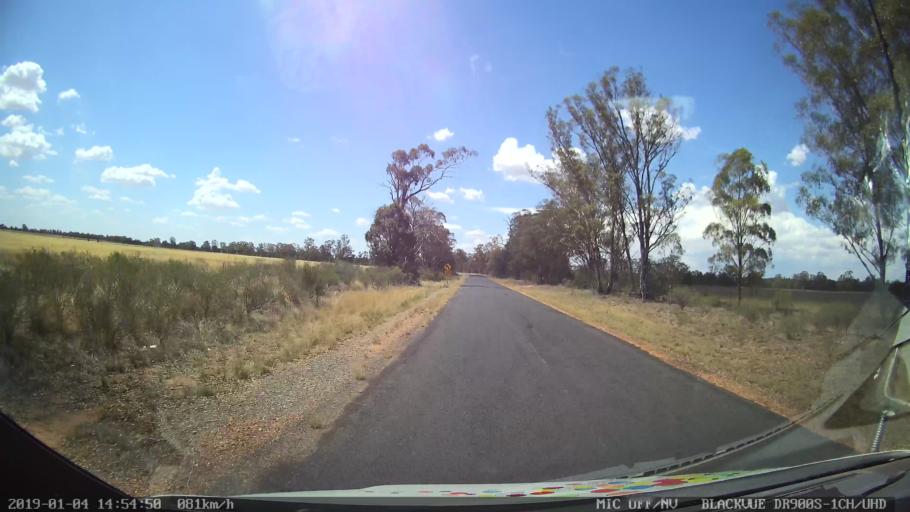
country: AU
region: New South Wales
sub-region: Dubbo Municipality
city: Dubbo
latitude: -31.9859
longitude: 148.6548
